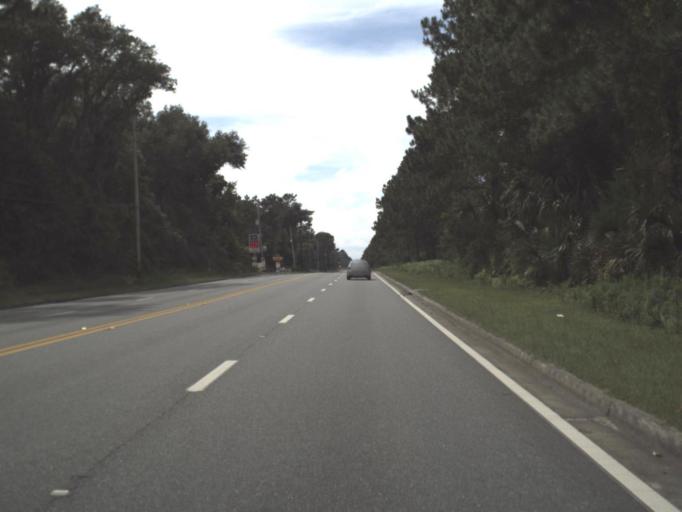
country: US
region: Florida
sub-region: Taylor County
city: Perry
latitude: 30.0969
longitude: -83.5480
